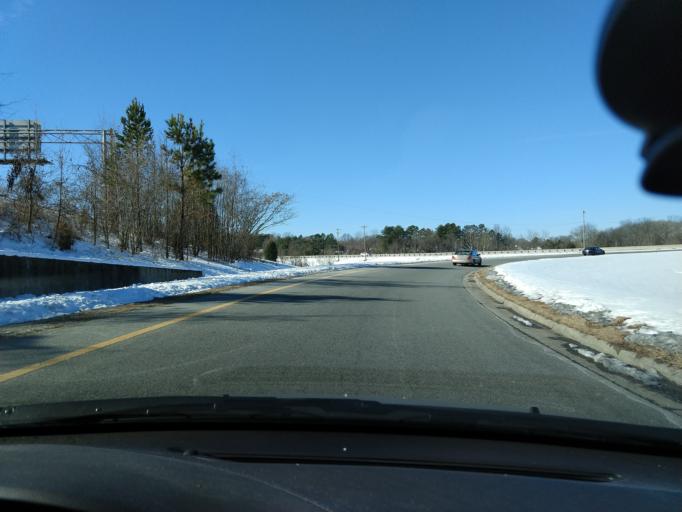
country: US
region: North Carolina
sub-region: Guilford County
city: Greensboro
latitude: 36.0337
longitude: -79.8187
